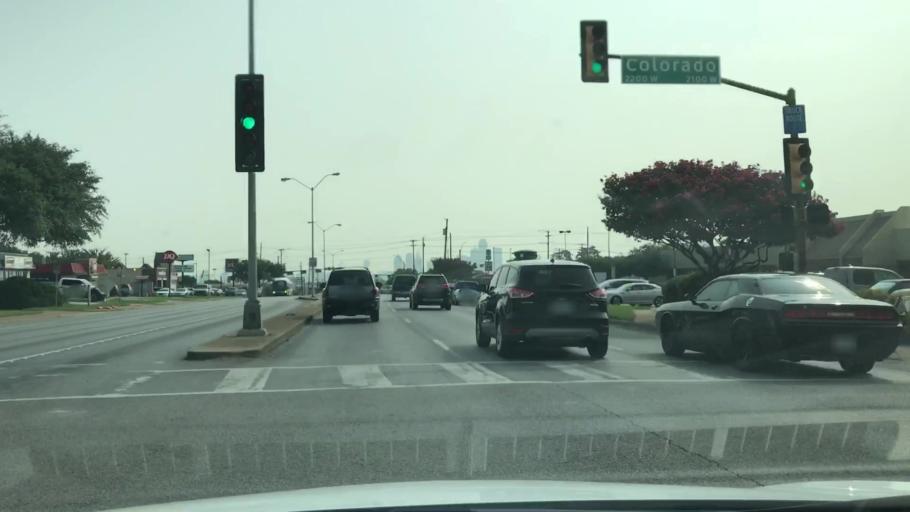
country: US
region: Texas
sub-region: Dallas County
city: Cockrell Hill
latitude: 32.7612
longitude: -96.8587
